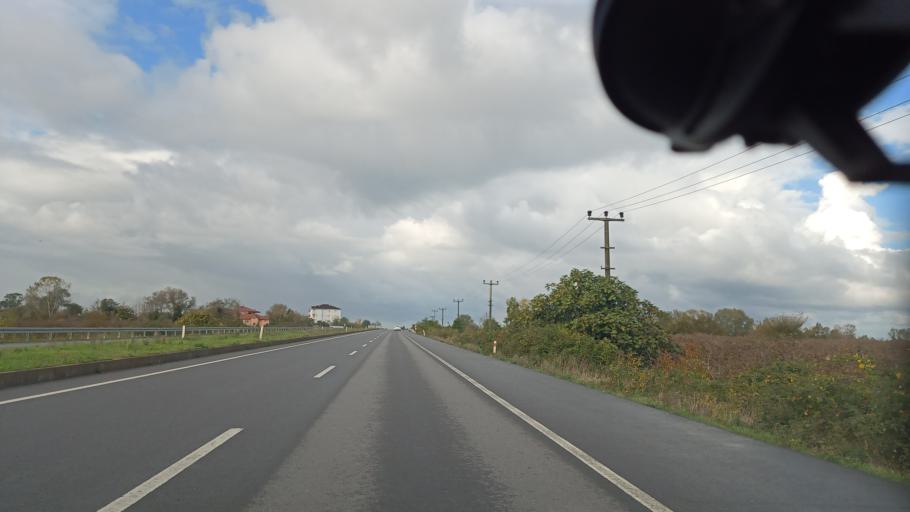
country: TR
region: Sakarya
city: Karasu
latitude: 41.0721
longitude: 30.7912
